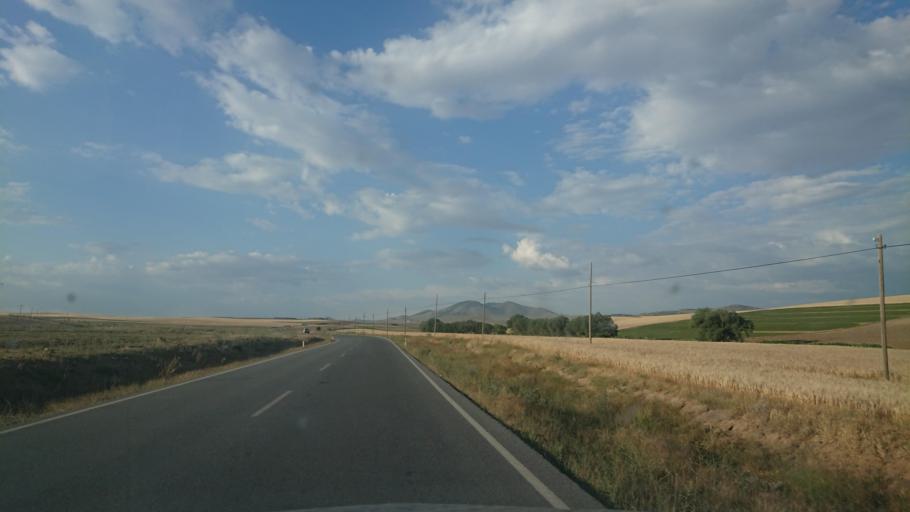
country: TR
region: Aksaray
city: Aksaray
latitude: 38.4831
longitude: 34.0655
